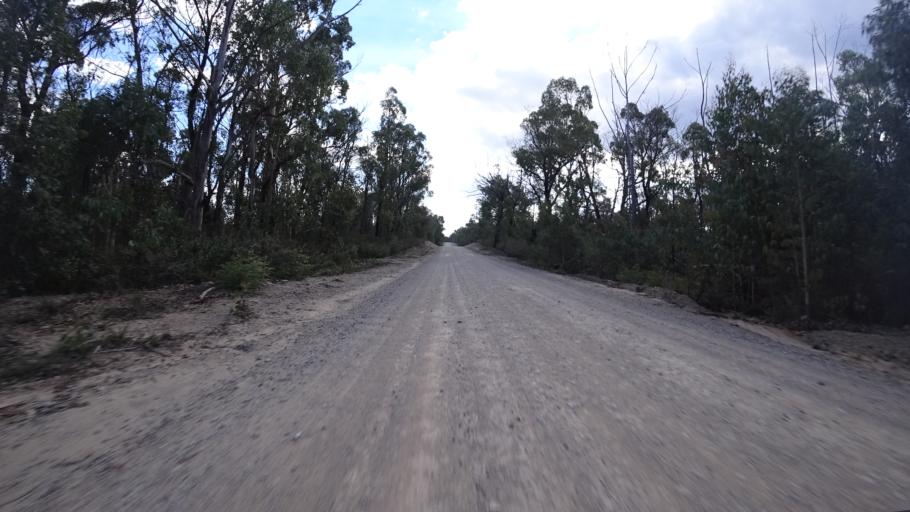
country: AU
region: New South Wales
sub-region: Lithgow
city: Lithgow
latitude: -33.4320
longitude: 150.1922
